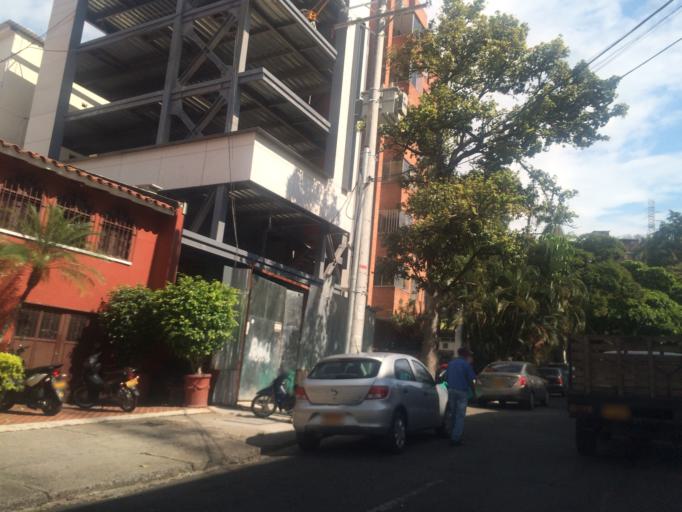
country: CO
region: Valle del Cauca
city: Cali
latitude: 3.4498
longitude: -76.5428
